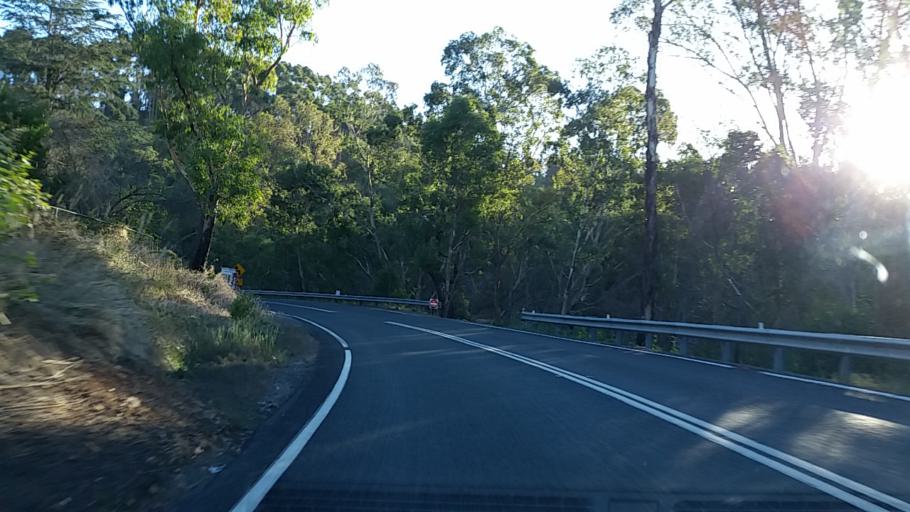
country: AU
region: South Australia
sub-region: Adelaide Hills
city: Gumeracha
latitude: -34.8219
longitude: 138.8519
